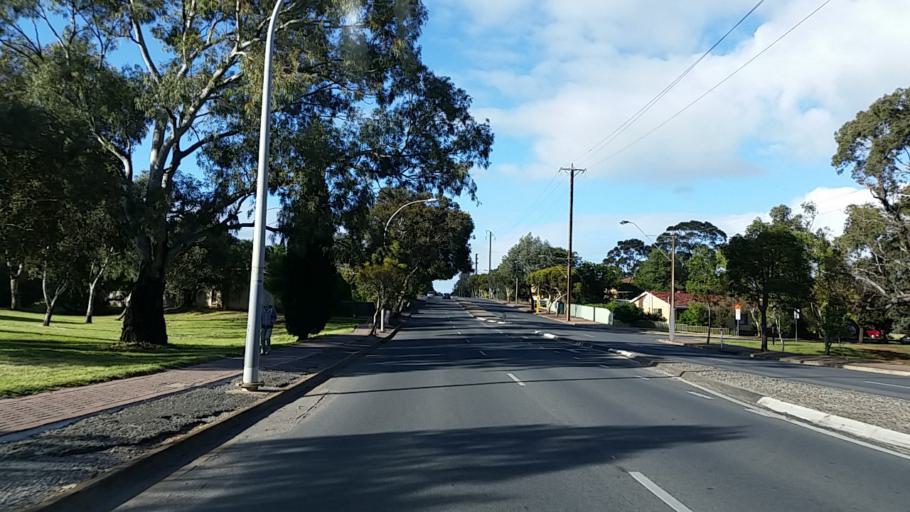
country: AU
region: South Australia
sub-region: Mitcham
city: Clapham
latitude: -35.0029
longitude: 138.5898
